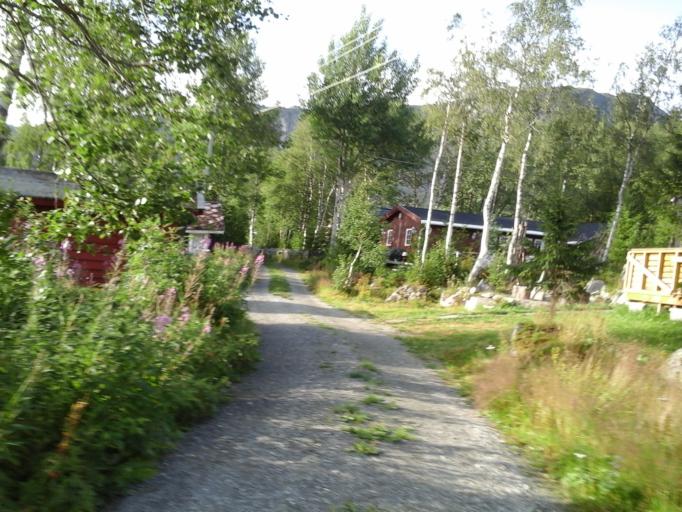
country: NO
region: Buskerud
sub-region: Hemsedal
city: Troim
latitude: 60.8437
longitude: 8.6192
